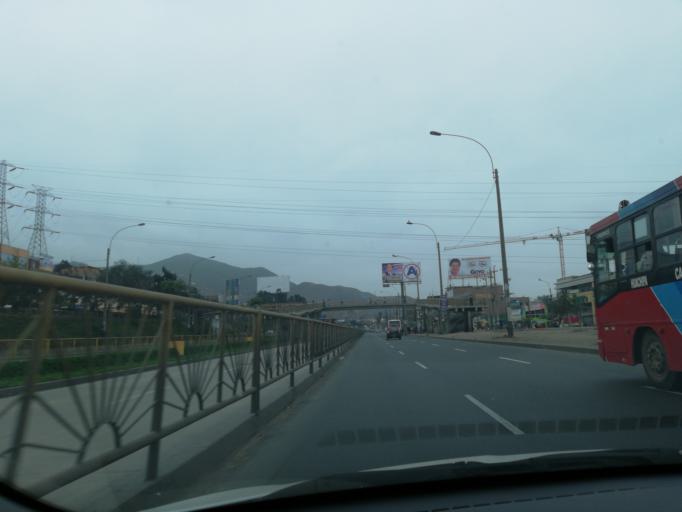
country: PE
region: Lima
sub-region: Lima
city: Independencia
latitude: -11.9935
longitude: -77.0570
